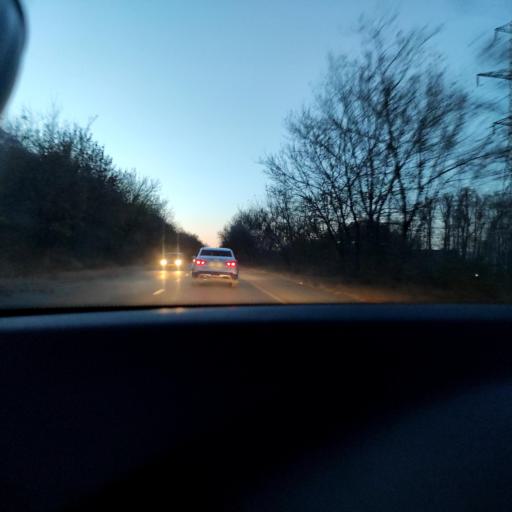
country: RU
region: Samara
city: Petra-Dubrava
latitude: 53.3113
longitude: 50.2749
